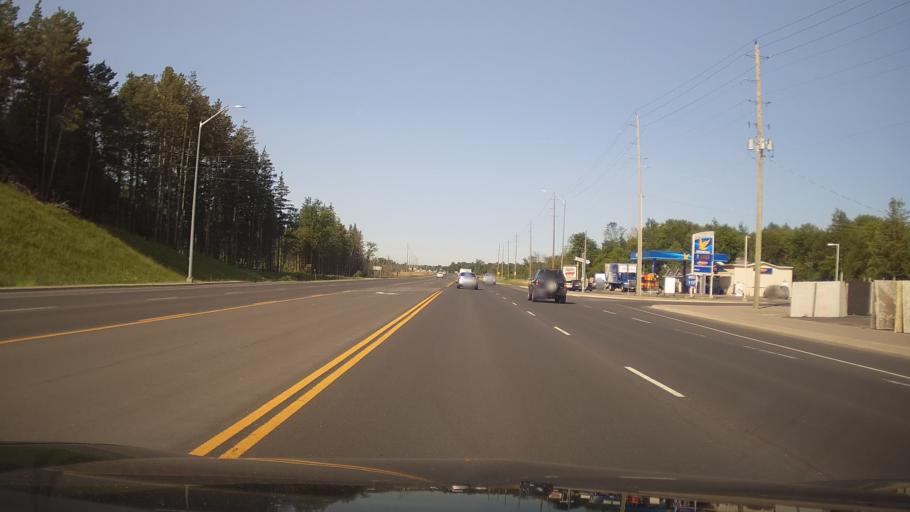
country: CA
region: Ontario
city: Peterborough
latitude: 44.3088
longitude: -78.2318
